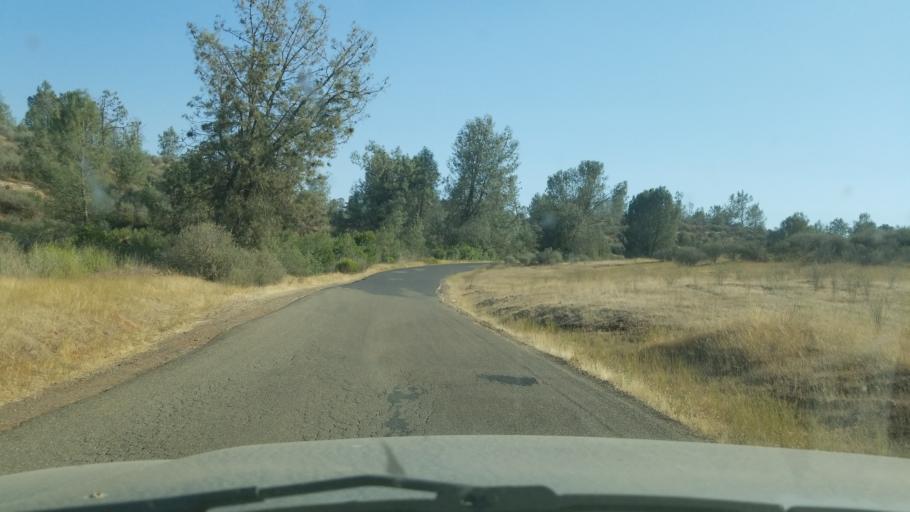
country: US
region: California
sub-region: Tuolumne County
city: Jamestown
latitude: 37.8465
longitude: -120.4624
